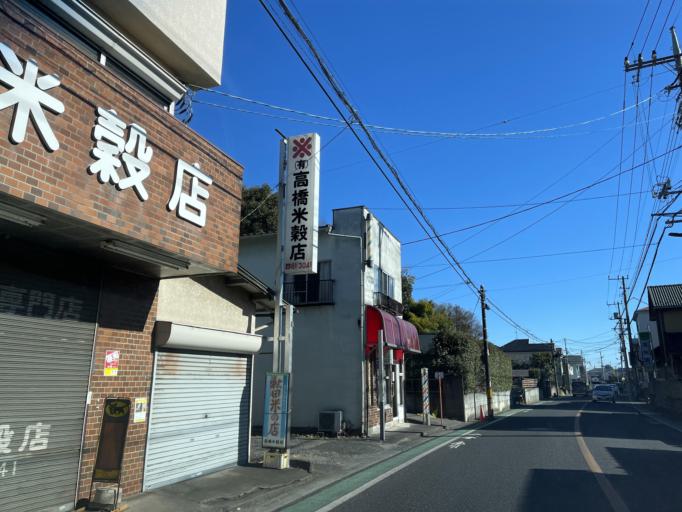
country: JP
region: Tokyo
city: Higashimurayama-shi
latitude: 35.7530
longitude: 139.4296
